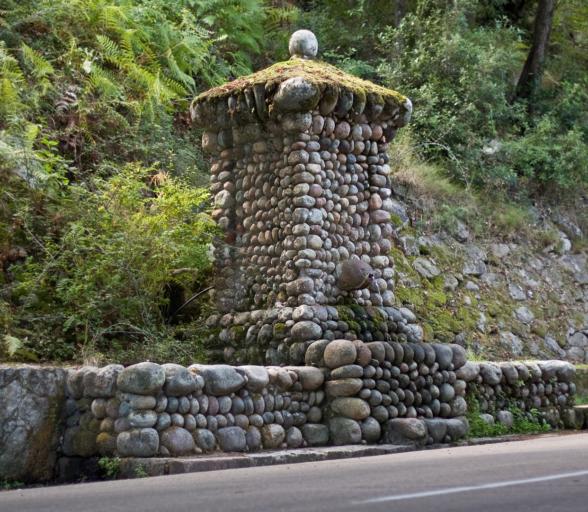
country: FR
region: Corsica
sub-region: Departement de la Corse-du-Sud
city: Cargese
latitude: 42.2598
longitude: 8.6799
